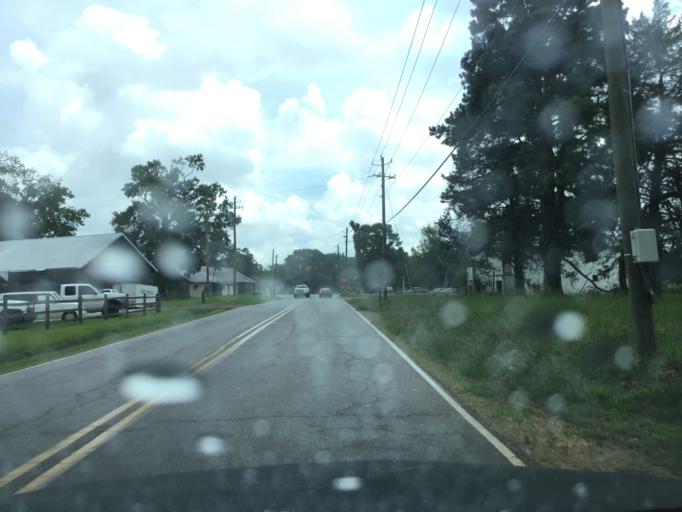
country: US
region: Alabama
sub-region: Montgomery County
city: Pike Road
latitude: 32.3632
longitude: -86.1029
